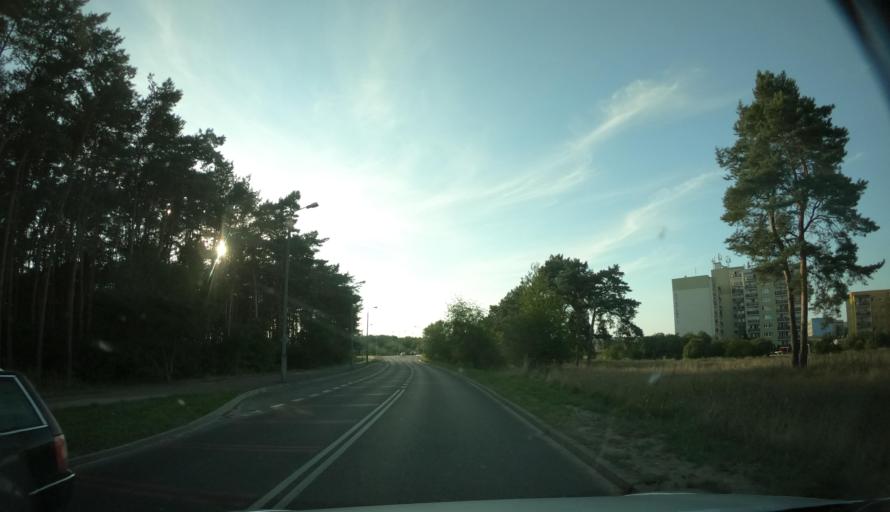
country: PL
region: Kujawsko-Pomorskie
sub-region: Bydgoszcz
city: Fordon
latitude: 53.1532
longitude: 18.1631
